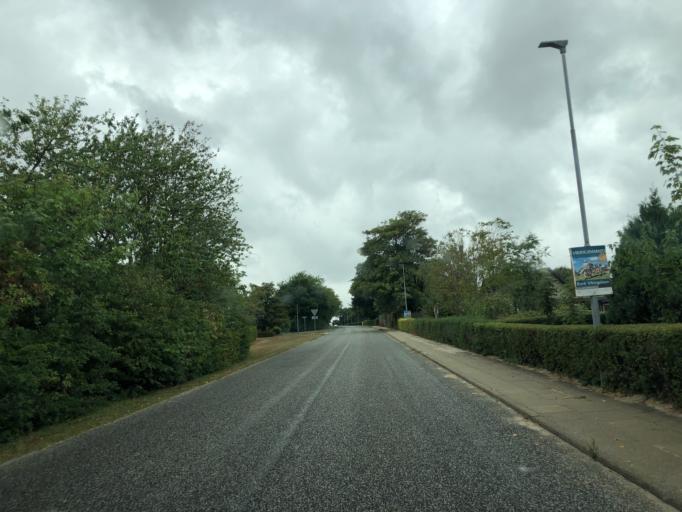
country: DK
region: Central Jutland
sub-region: Ringkobing-Skjern Kommune
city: Videbaek
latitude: 56.1235
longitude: 8.5026
